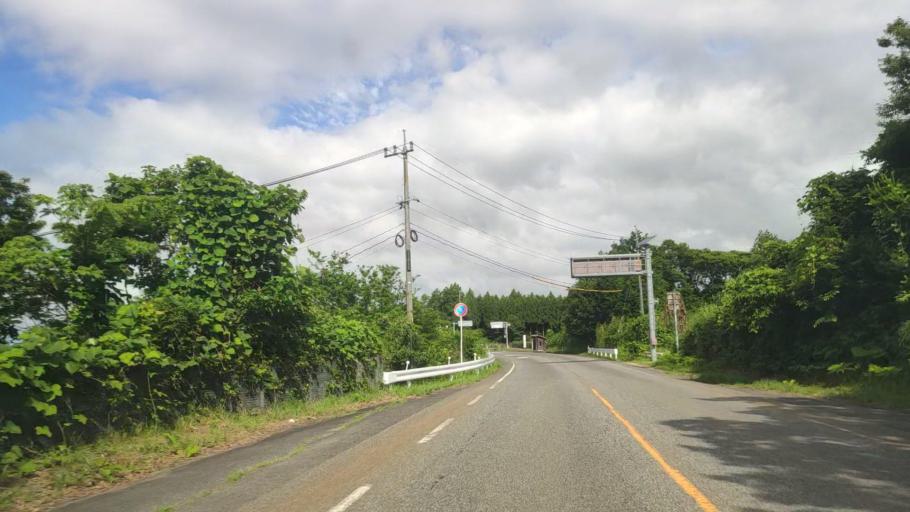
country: JP
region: Tottori
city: Yonago
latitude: 35.4182
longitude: 133.4555
